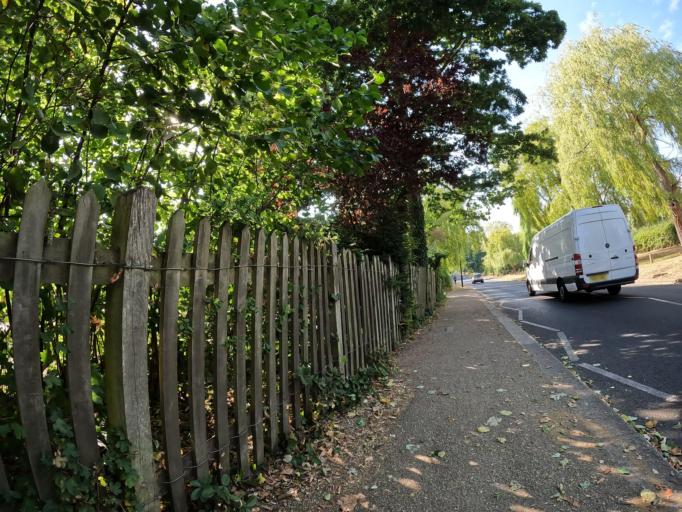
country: GB
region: England
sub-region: Hertfordshire
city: Potters Bar
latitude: 51.6904
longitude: -0.1574
